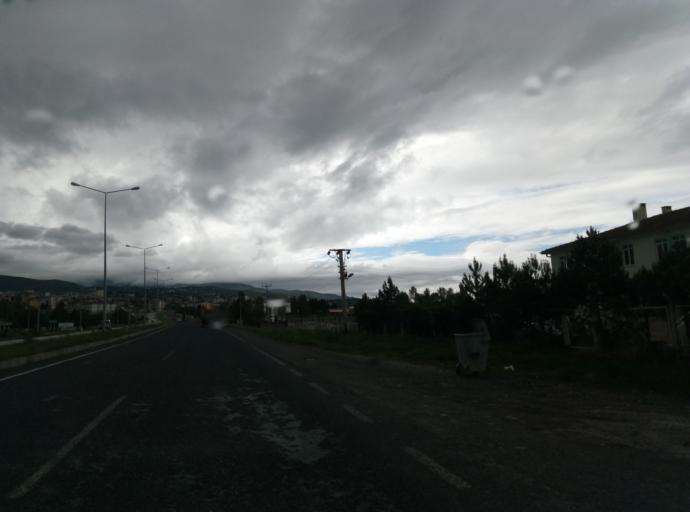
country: TR
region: Sivas
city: Susehri
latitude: 40.1701
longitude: 38.1070
